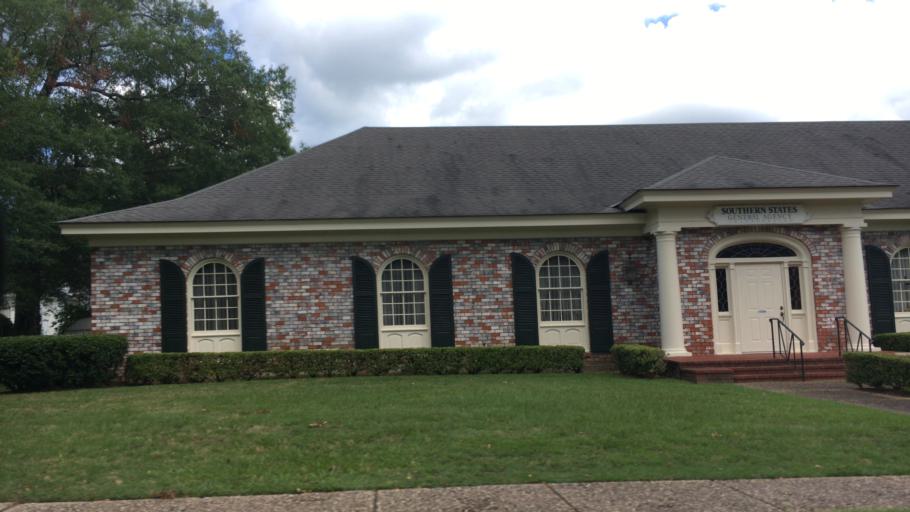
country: US
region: Louisiana
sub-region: Lincoln Parish
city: Ruston
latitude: 32.5339
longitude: -92.6389
